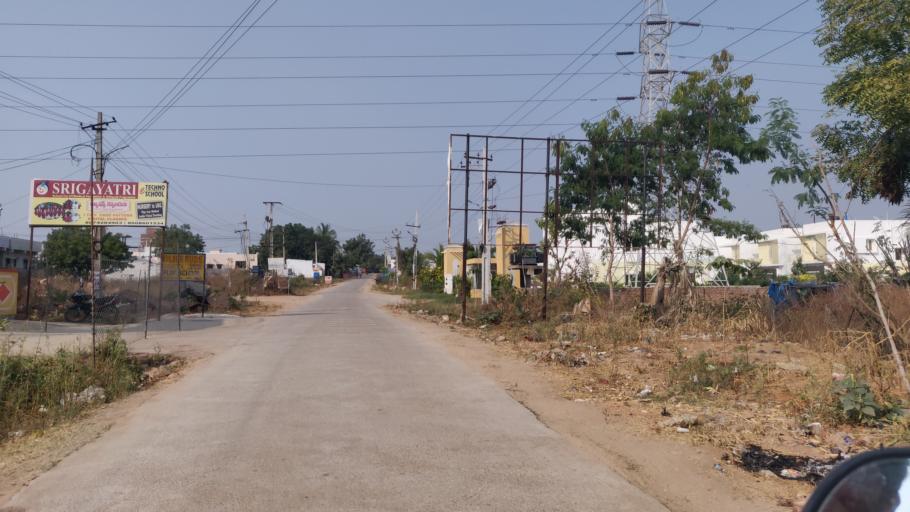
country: IN
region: Telangana
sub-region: Rangareddi
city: Uppal Kalan
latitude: 17.3962
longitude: 78.6050
